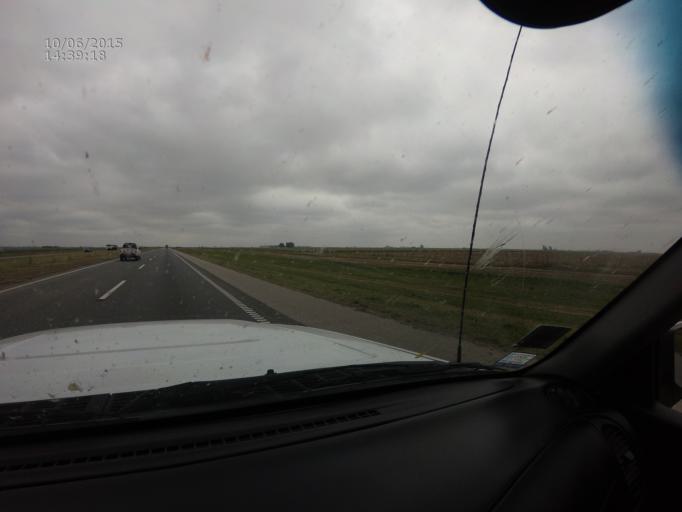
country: AR
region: Cordoba
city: James Craik
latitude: -32.0794
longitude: -63.4854
